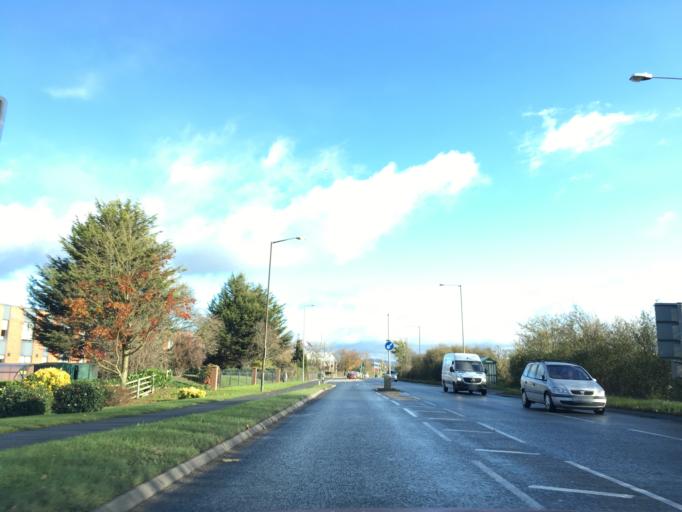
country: GB
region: England
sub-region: Worcestershire
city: Bredon
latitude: 51.9966
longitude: -2.1212
